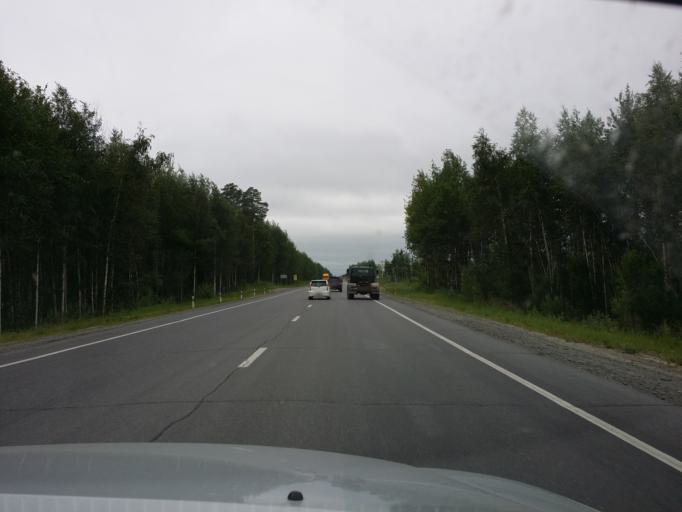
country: RU
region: Khanty-Mansiyskiy Avtonomnyy Okrug
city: Megion
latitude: 61.0615
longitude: 76.2793
